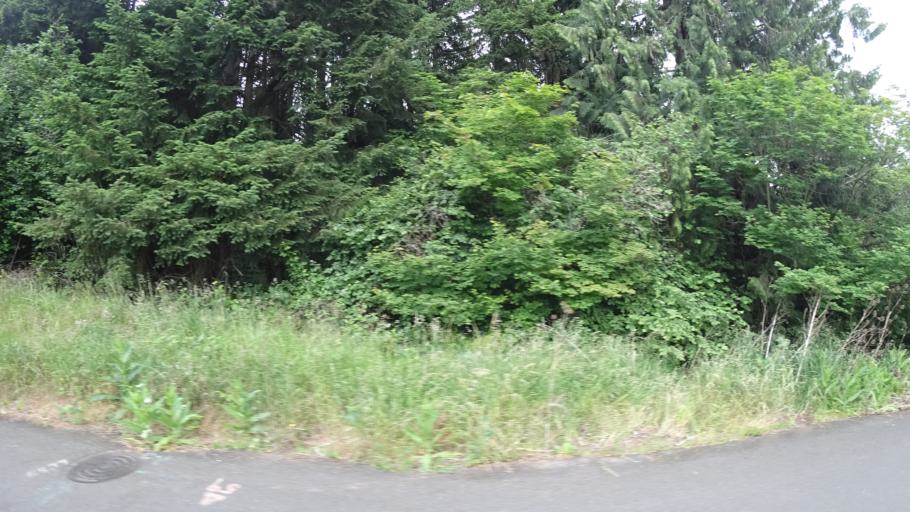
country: US
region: Oregon
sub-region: Clackamas County
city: Happy Valley
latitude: 45.4810
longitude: -122.5147
